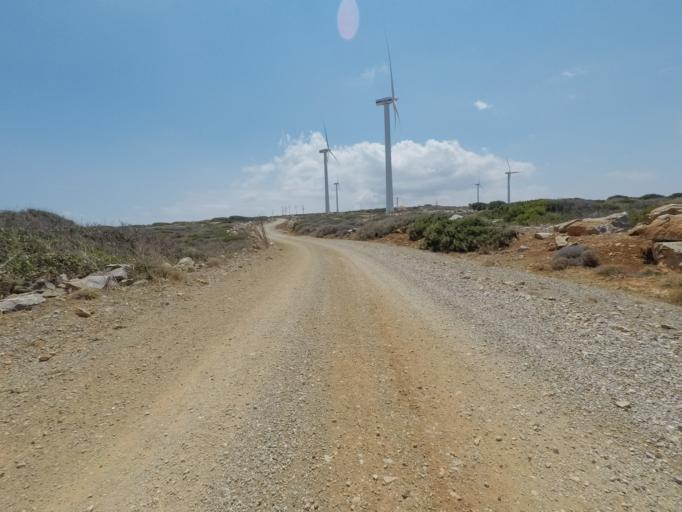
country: GR
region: Crete
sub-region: Nomos Lasithiou
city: Elounda
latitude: 35.3275
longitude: 25.7564
